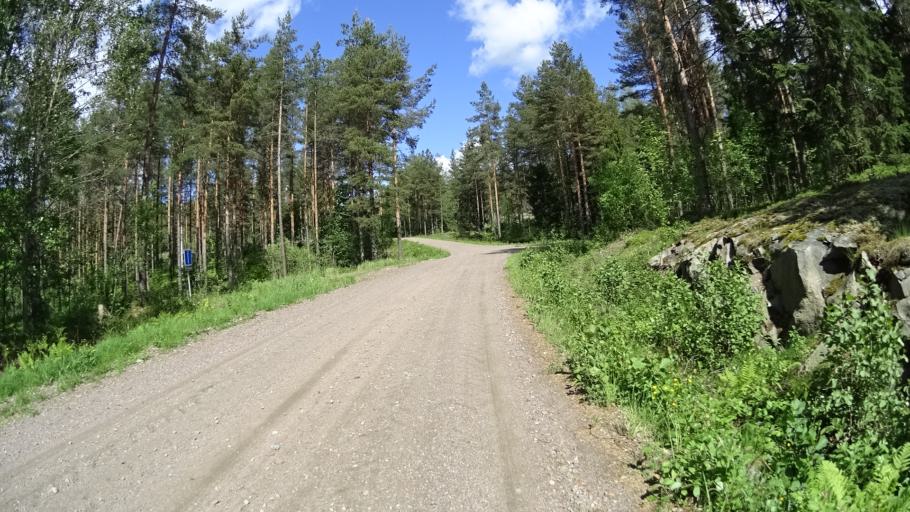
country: FI
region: Uusimaa
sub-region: Raaseporin
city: Karis
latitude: 60.1314
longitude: 23.6184
